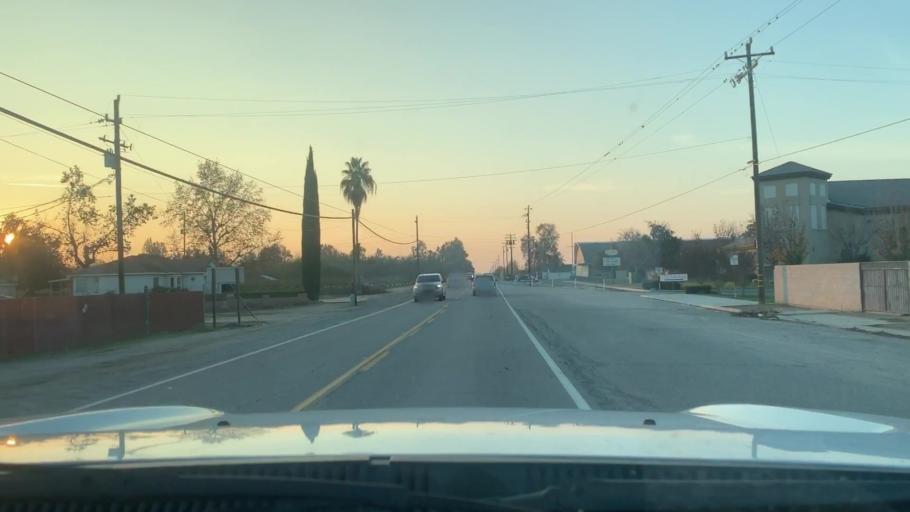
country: US
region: California
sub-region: Kern County
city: Rosedale
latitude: 35.3835
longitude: -119.2030
